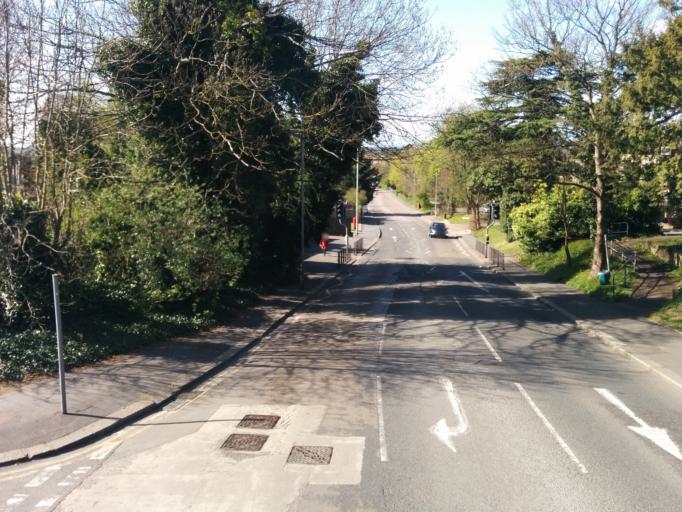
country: GB
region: England
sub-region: Hertfordshire
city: Bushey
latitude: 51.6402
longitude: -0.3569
